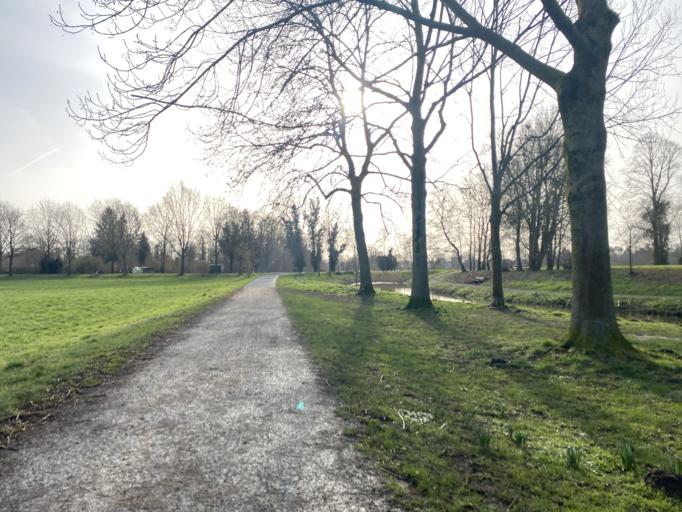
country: DE
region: North Rhine-Westphalia
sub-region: Regierungsbezirk Arnsberg
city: Hamm
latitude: 51.6832
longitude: 7.8468
